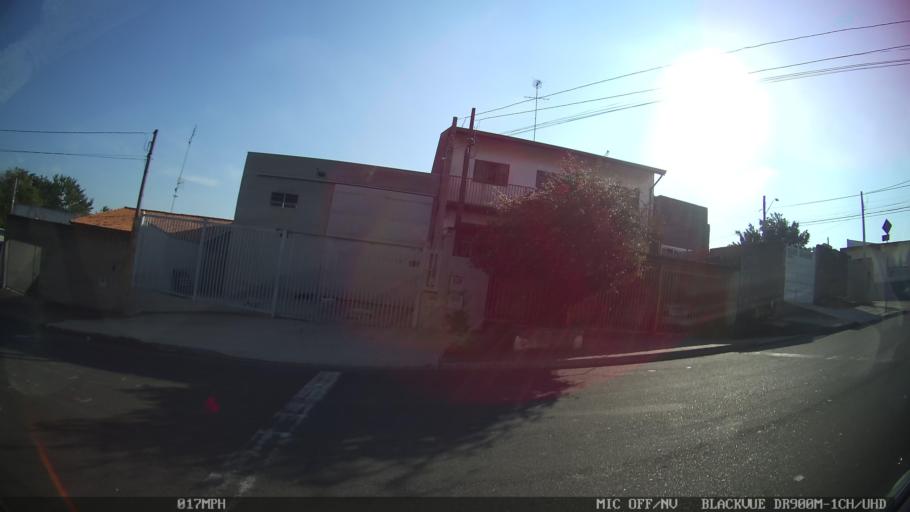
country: BR
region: Sao Paulo
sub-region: Campinas
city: Campinas
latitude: -22.9905
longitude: -47.1416
